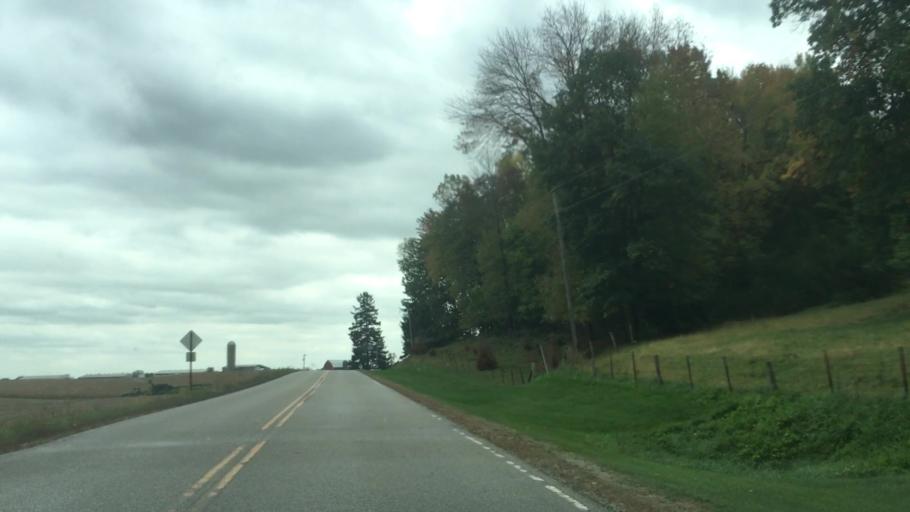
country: US
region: Minnesota
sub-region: Fillmore County
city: Preston
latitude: 43.7403
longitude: -92.0099
